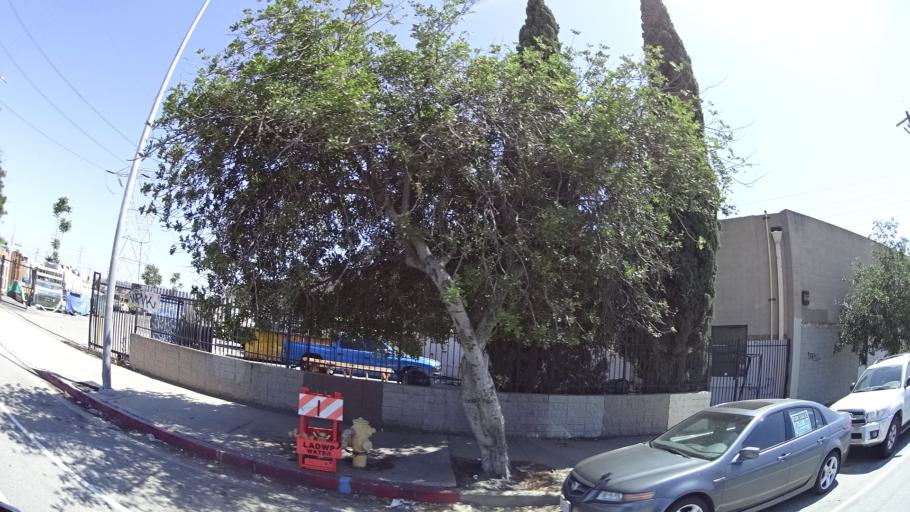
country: US
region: California
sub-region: Los Angeles County
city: North Hollywood
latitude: 34.2012
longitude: -118.3903
